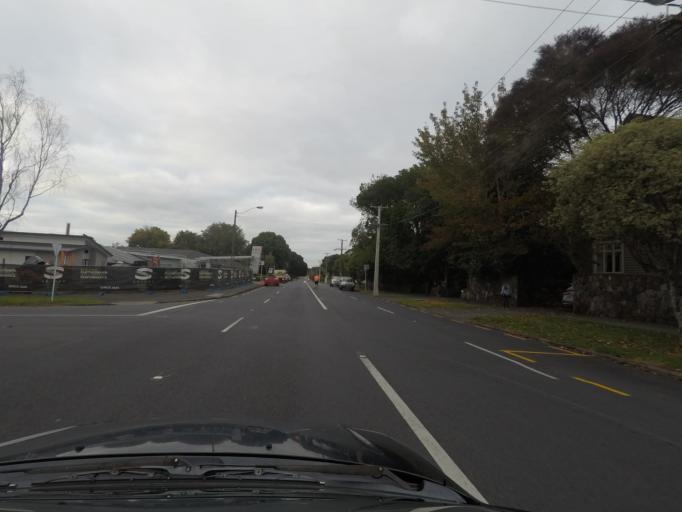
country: NZ
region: Auckland
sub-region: Auckland
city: Auckland
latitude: -36.8804
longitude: 174.7721
